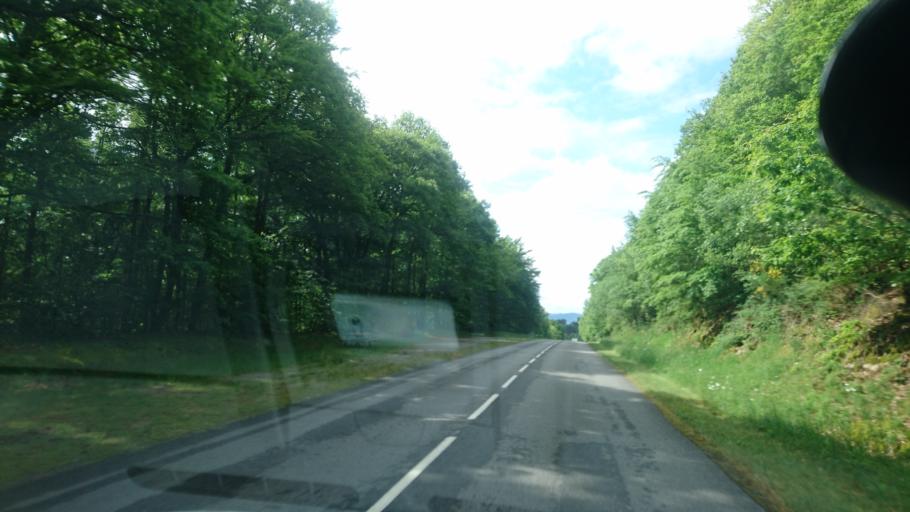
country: FR
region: Limousin
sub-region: Departement de la Haute-Vienne
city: Peyrat-le-Chateau
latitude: 45.7870
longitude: 1.8493
